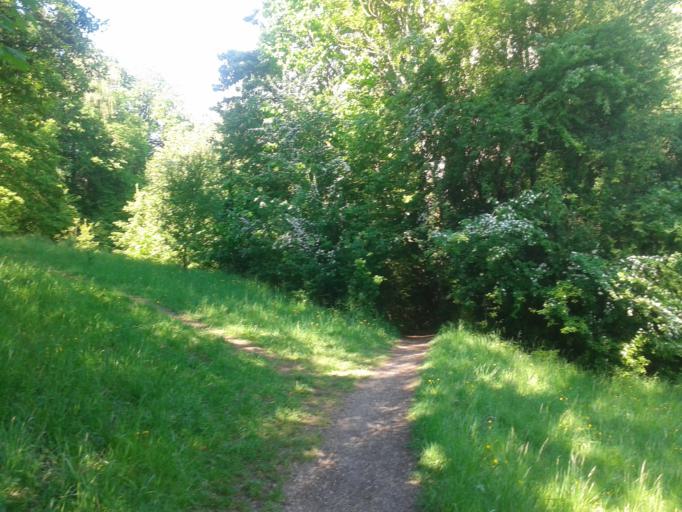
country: DE
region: Bavaria
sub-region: Upper Franconia
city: Stegaurach
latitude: 49.8834
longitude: 10.8677
